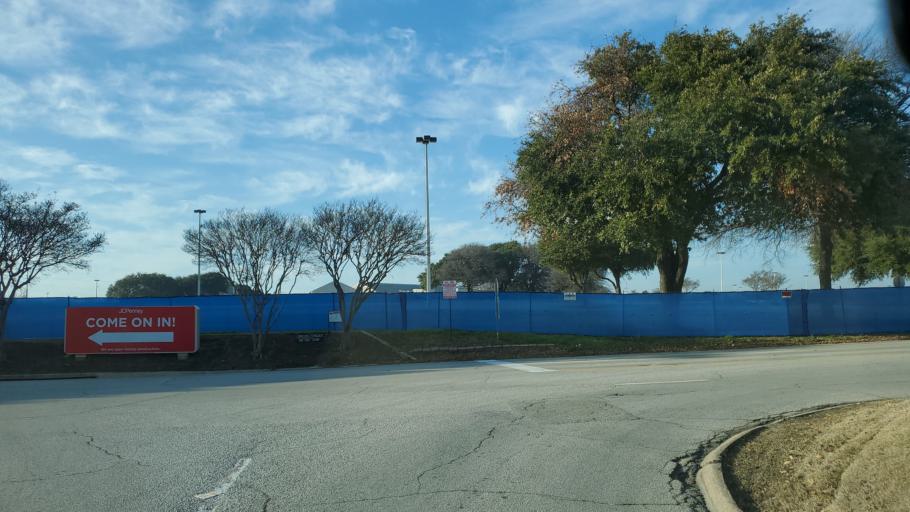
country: US
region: Texas
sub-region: Collin County
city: Plano
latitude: 33.0107
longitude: -96.7105
